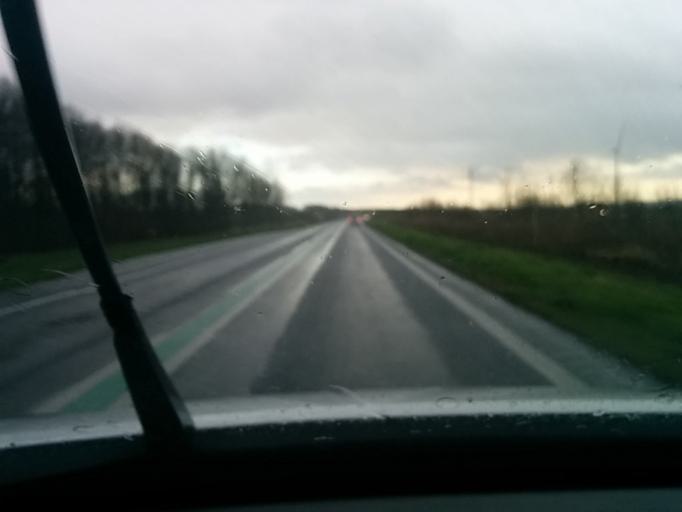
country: NL
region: Utrecht
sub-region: Gemeente Bunschoten
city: Bunschoten
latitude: 52.3142
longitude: 5.4408
